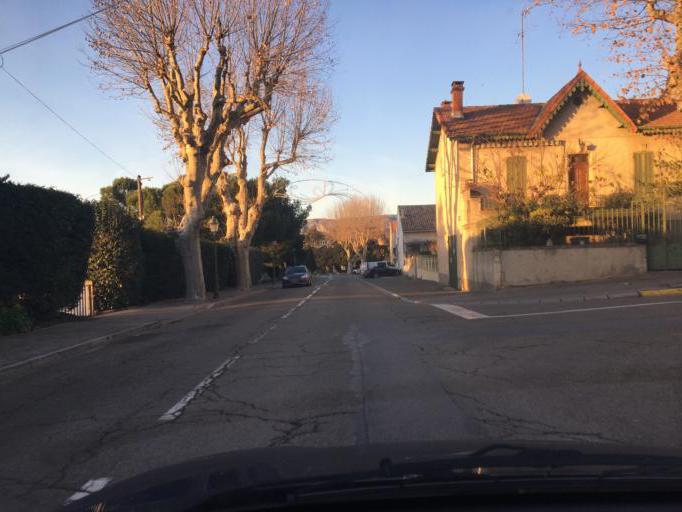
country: FR
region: Provence-Alpes-Cote d'Azur
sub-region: Departement des Bouches-du-Rhone
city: Mallemort
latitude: 43.7305
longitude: 5.1773
